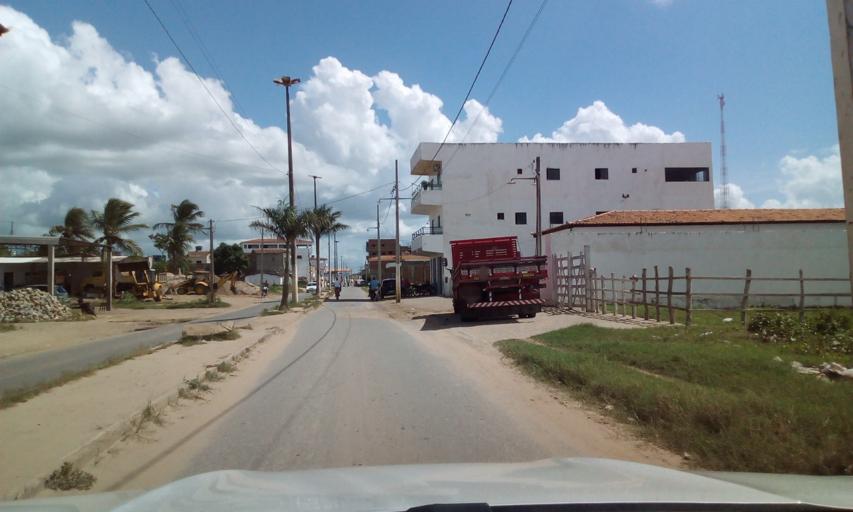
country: BR
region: Paraiba
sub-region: Guarabira
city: Guarabira
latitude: -6.8508
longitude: -35.3784
